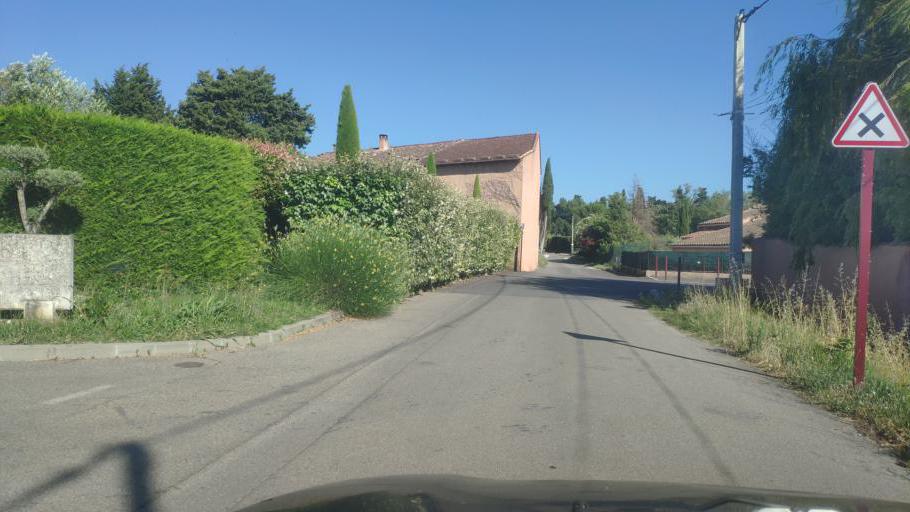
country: FR
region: Provence-Alpes-Cote d'Azur
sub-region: Departement du Vaucluse
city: Aubignan
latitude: 44.0900
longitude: 5.0372
